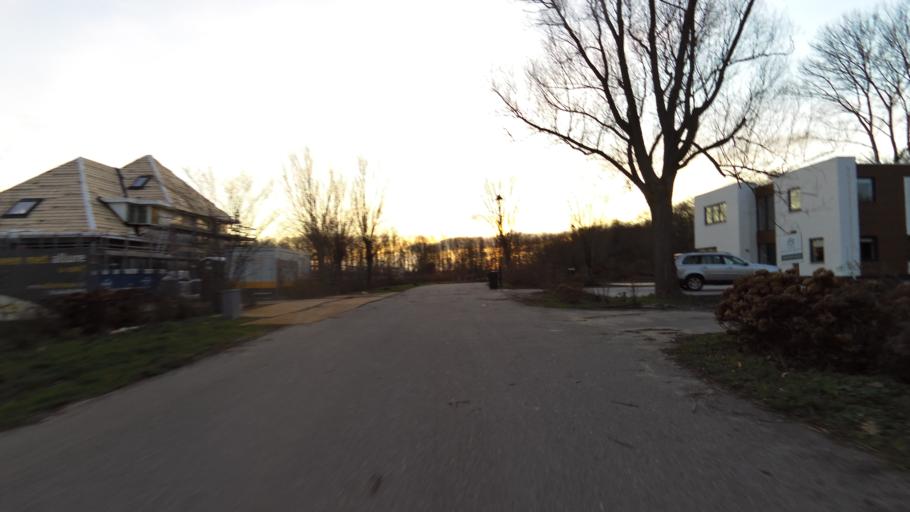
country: NL
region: South Holland
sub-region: Gemeente Noordwijkerhout
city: Noordwijkerhout
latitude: 52.2762
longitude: 4.4916
